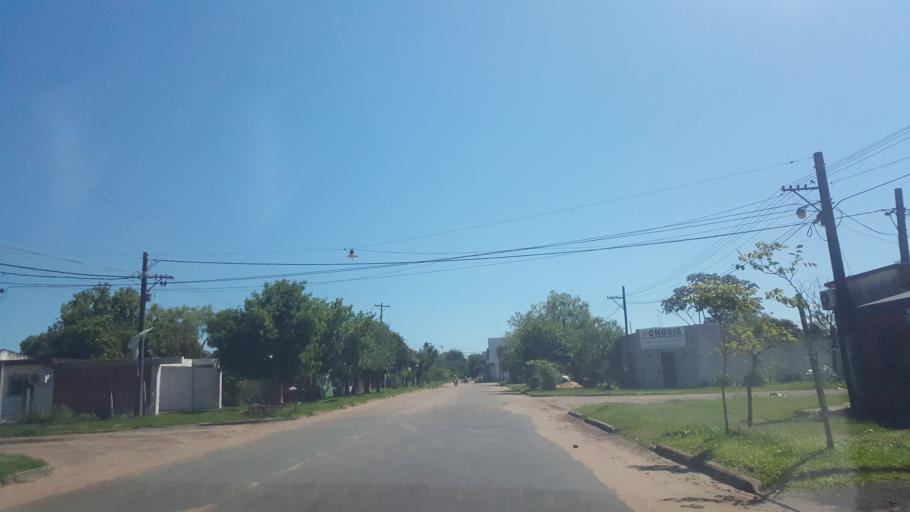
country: AR
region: Corrientes
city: Ituzaingo
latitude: -27.5949
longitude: -56.6958
